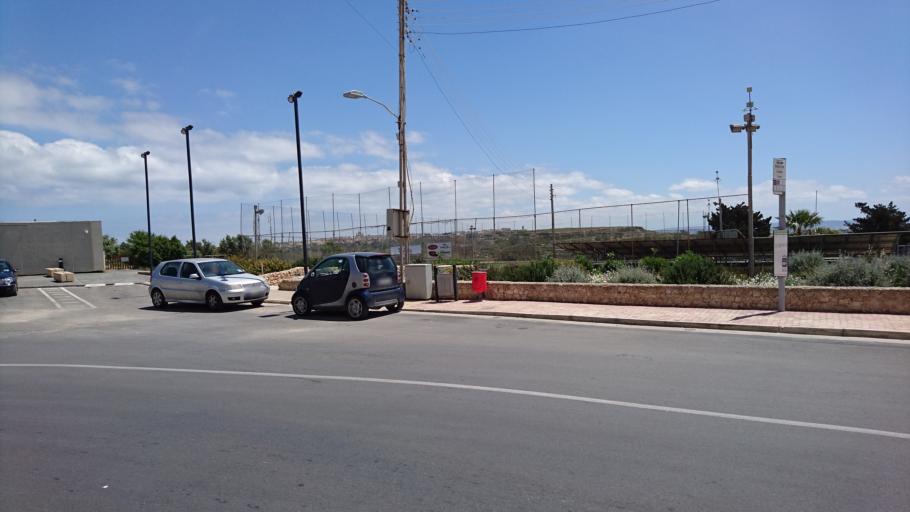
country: MT
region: Ix-Xaghra
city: Xaghra
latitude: 36.0475
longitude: 14.2666
